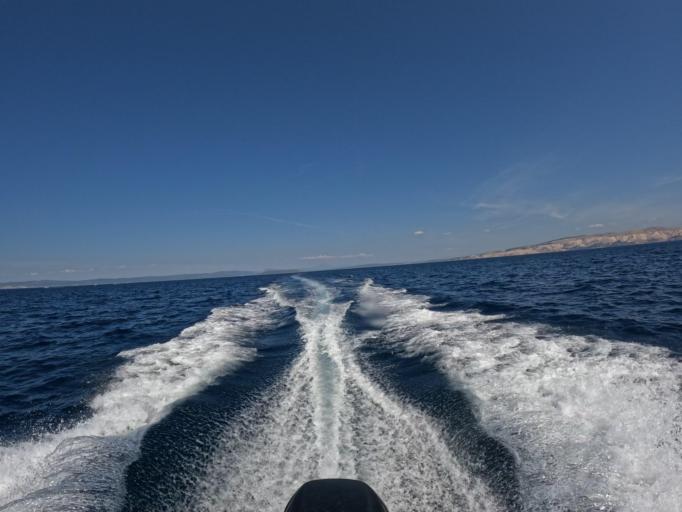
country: HR
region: Primorsko-Goranska
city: Lopar
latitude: 44.8810
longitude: 14.6571
